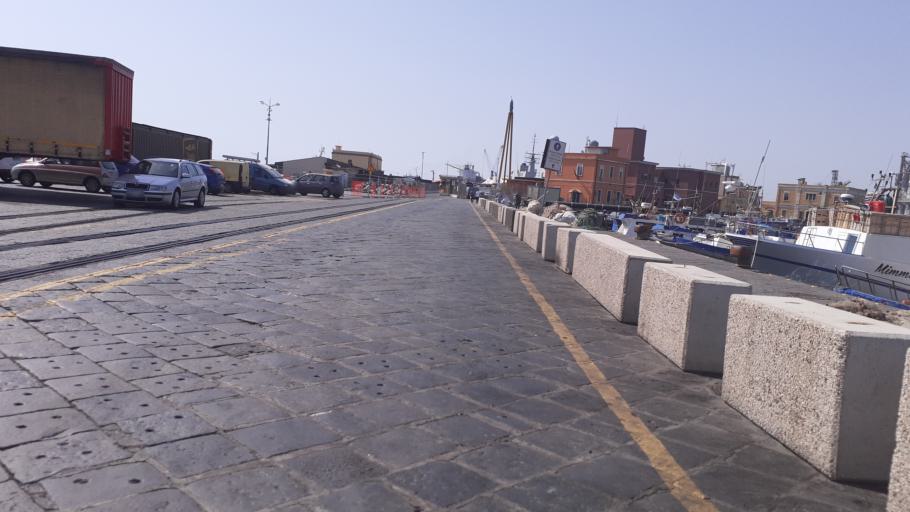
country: IT
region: Sicily
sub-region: Catania
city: Catania
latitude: 37.4998
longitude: 15.0945
